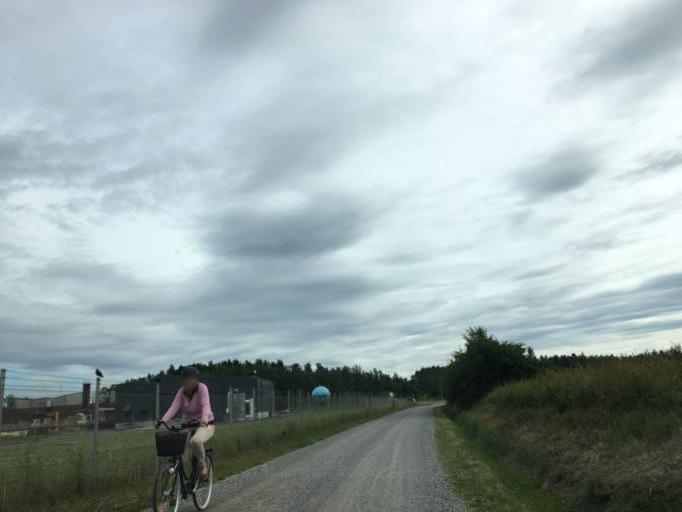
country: SE
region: Soedermanland
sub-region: Eskilstuna Kommun
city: Torshalla
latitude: 59.3868
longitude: 16.4585
